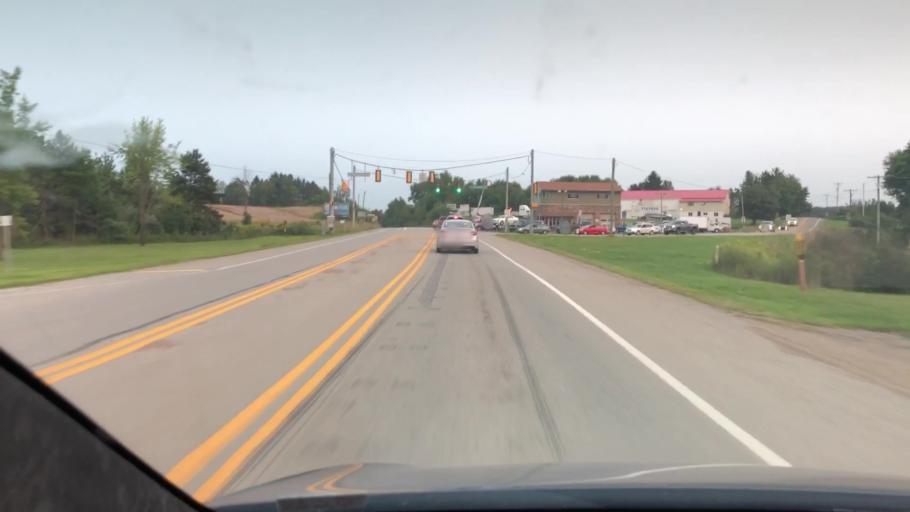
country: US
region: Pennsylvania
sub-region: Butler County
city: Shanor-Northvue
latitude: 40.9215
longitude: -79.9478
